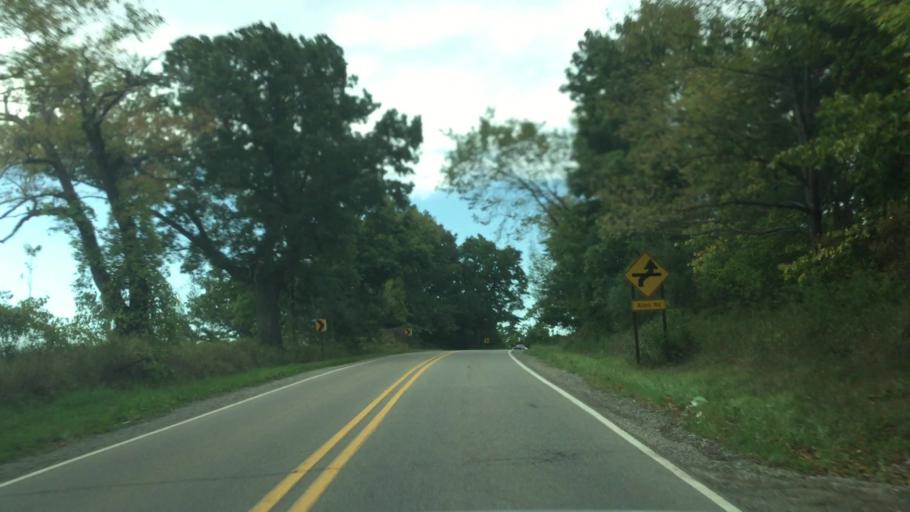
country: US
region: Michigan
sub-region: Genesee County
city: Argentine
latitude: 42.6922
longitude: -83.8382
